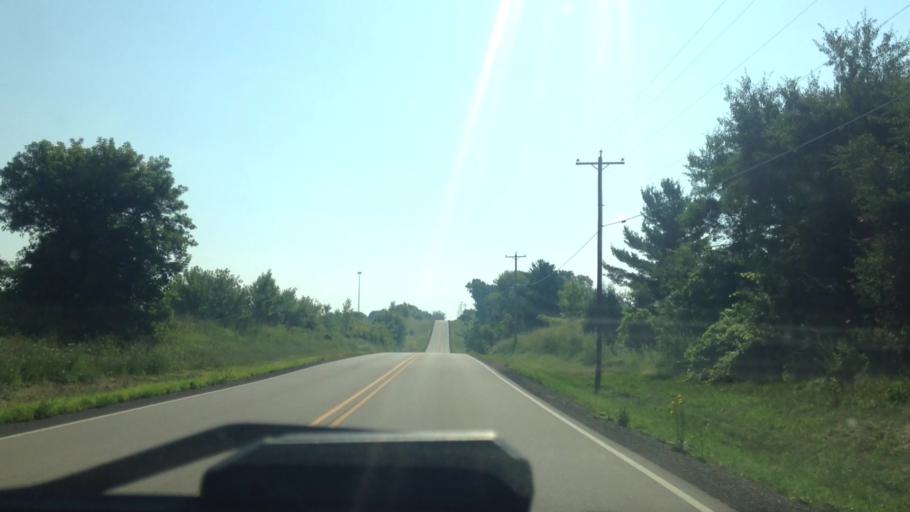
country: US
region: Wisconsin
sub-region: Waukesha County
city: Merton
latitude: 43.1631
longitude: -88.2761
